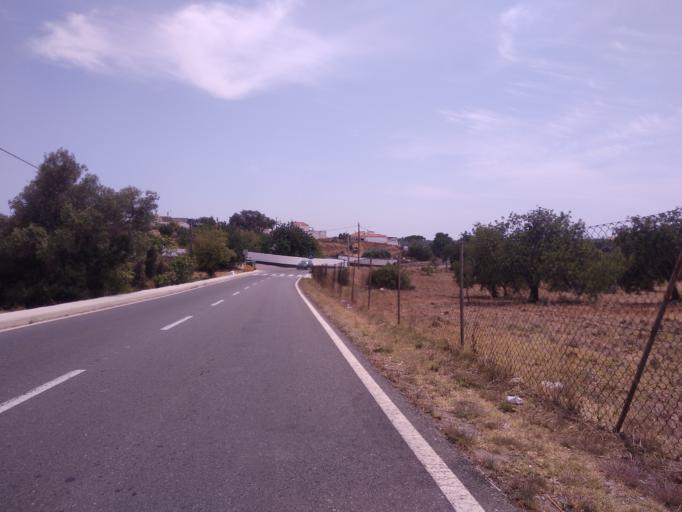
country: PT
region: Faro
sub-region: Faro
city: Santa Barbara de Nexe
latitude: 37.0853
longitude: -7.9934
